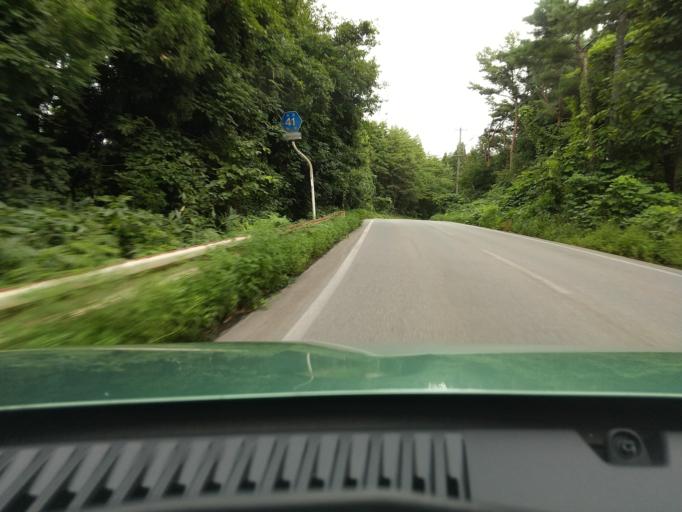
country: JP
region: Akita
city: Akita
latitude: 39.7717
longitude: 140.1337
